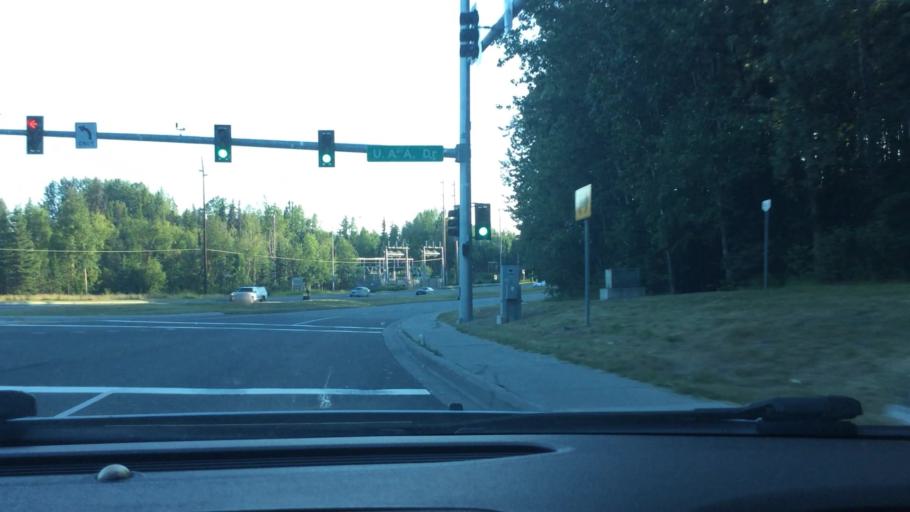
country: US
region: Alaska
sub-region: Anchorage Municipality
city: Anchorage
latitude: 61.1960
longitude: -149.8275
